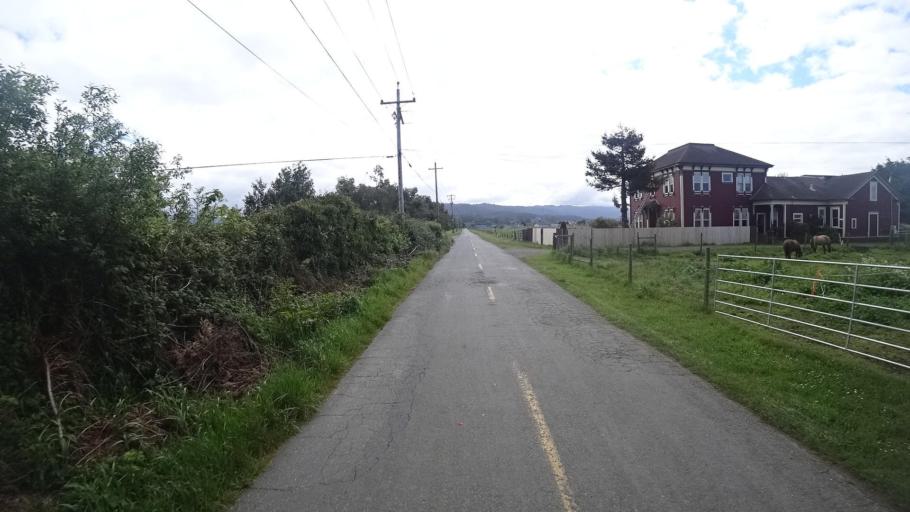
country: US
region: California
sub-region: Humboldt County
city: Arcata
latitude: 40.8830
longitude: -124.1075
